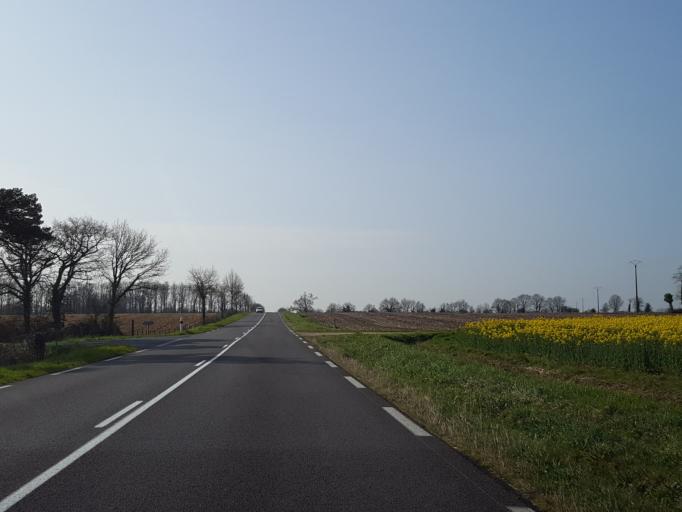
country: FR
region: Pays de la Loire
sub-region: Departement de la Vendee
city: Les Lucs-sur-Boulogne
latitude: 46.8744
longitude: -1.4998
